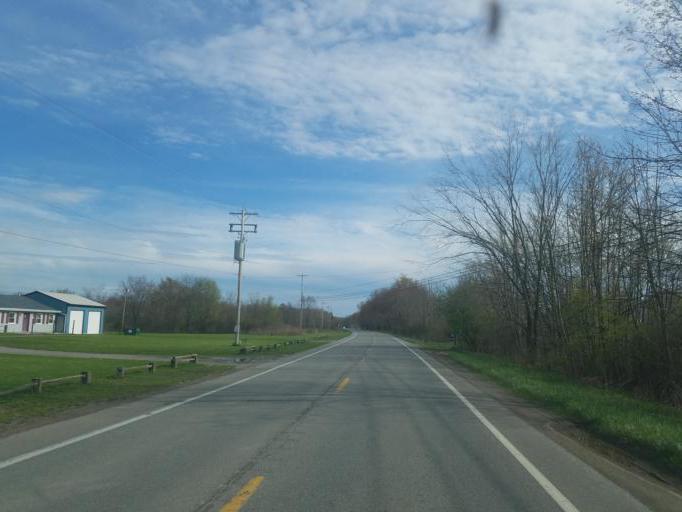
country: US
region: Pennsylvania
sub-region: Mercer County
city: Stoneboro
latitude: 41.3967
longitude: -80.0736
